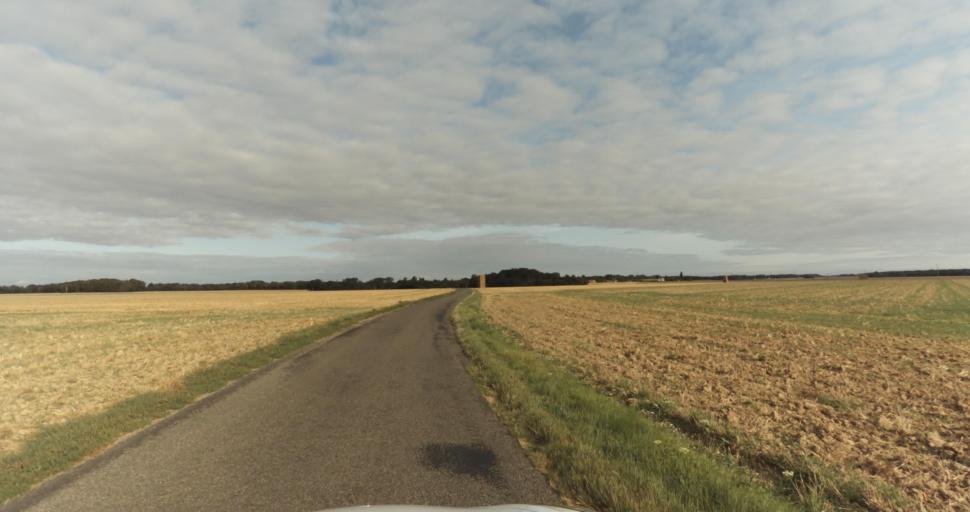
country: FR
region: Centre
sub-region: Departement d'Eure-et-Loir
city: Saint-Remy-sur-Avre
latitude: 48.8082
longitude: 1.2473
